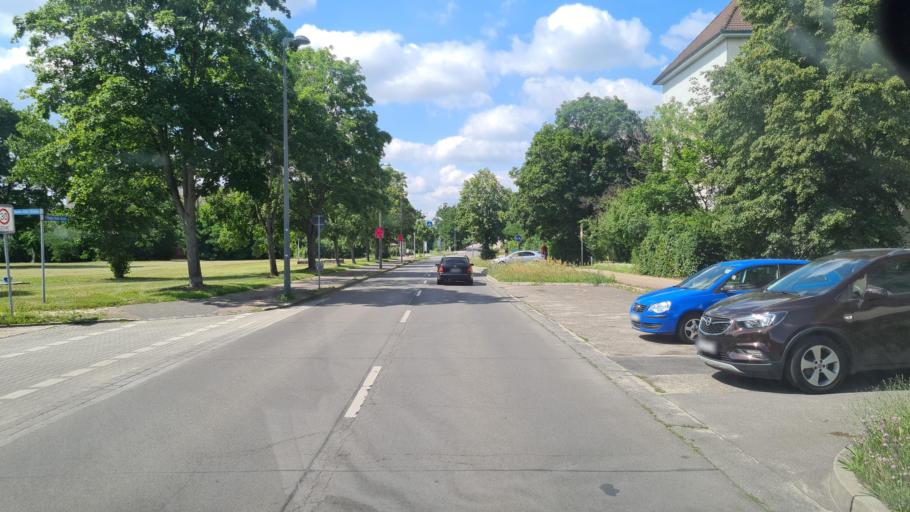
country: DE
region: Brandenburg
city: Senftenberg
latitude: 51.5144
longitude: 13.9851
